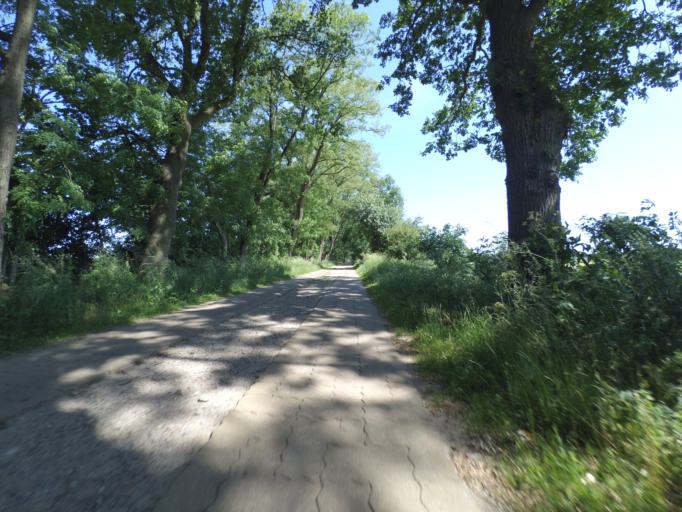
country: DE
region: Brandenburg
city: Pritzwalk
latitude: 53.1282
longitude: 12.2362
